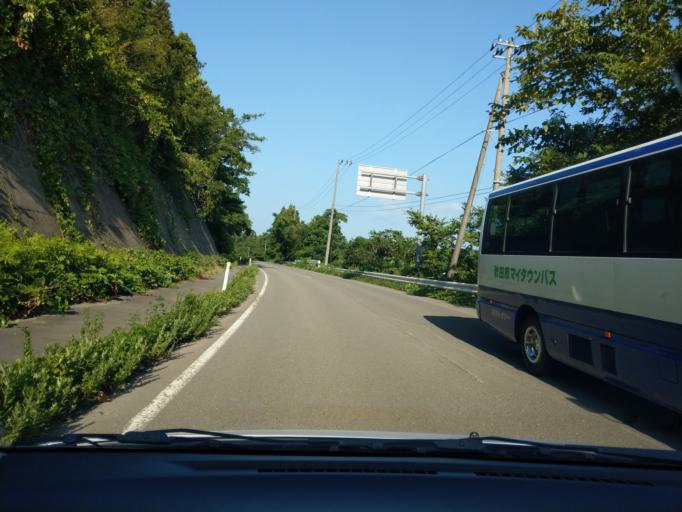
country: JP
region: Akita
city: Akita
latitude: 39.6000
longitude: 140.2069
